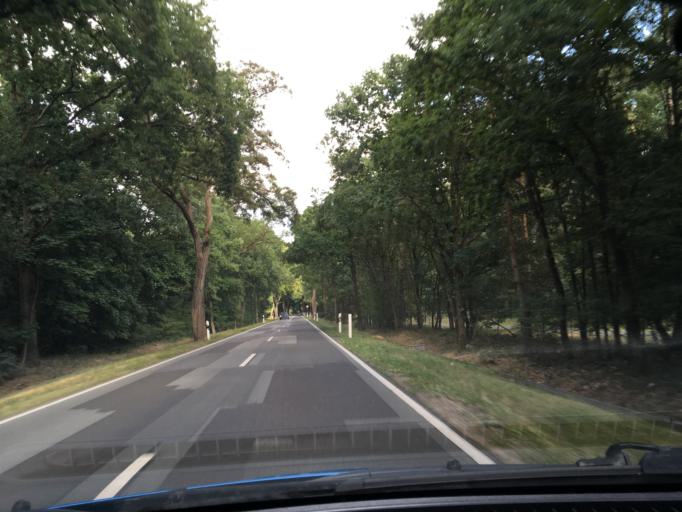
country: DE
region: Mecklenburg-Vorpommern
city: Domitz
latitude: 53.1531
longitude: 11.2277
